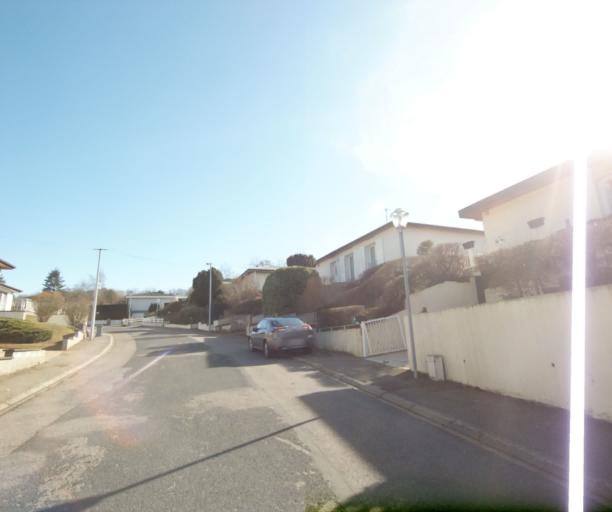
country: FR
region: Lorraine
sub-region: Departement de Meurthe-et-Moselle
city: Villers-les-Nancy
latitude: 48.6733
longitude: 6.1409
